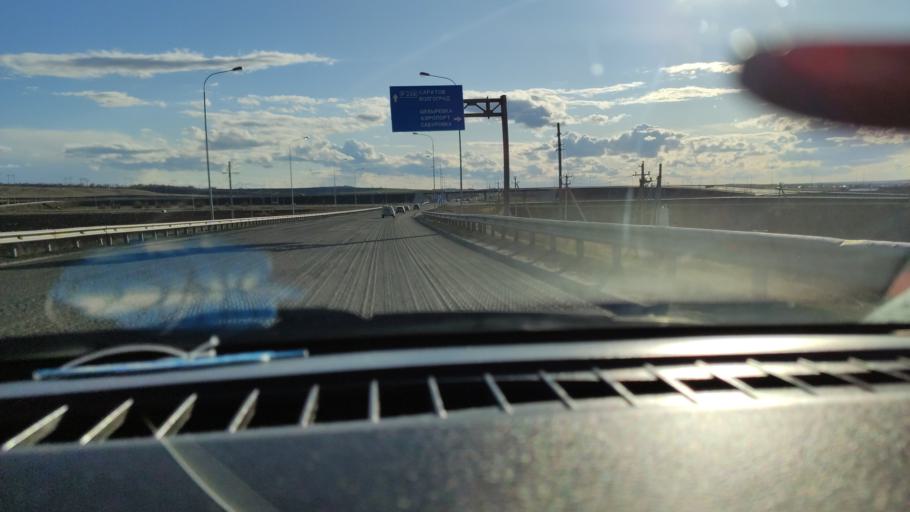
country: RU
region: Saratov
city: Yelshanka
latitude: 51.7973
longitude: 46.1780
